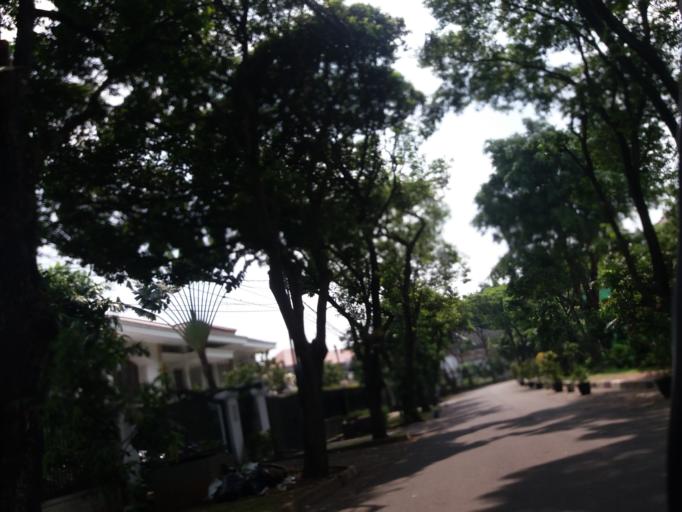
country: ID
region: Jakarta Raya
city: Jakarta
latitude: -6.2341
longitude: 106.8021
